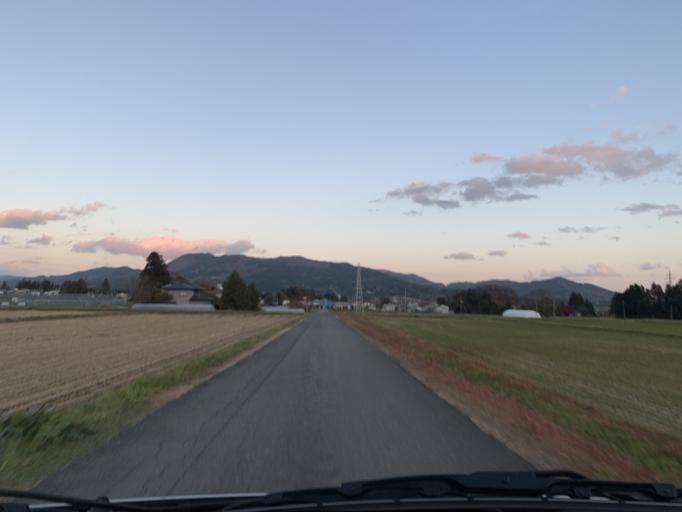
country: JP
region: Iwate
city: Ichinoseki
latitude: 39.0120
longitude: 141.1039
